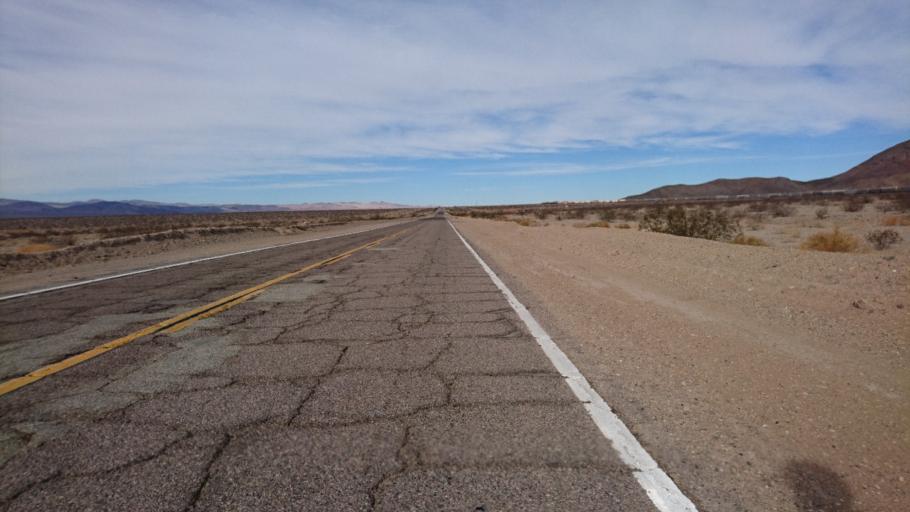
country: US
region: California
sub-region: San Bernardino County
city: Twentynine Palms
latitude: 34.5969
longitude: -115.9343
